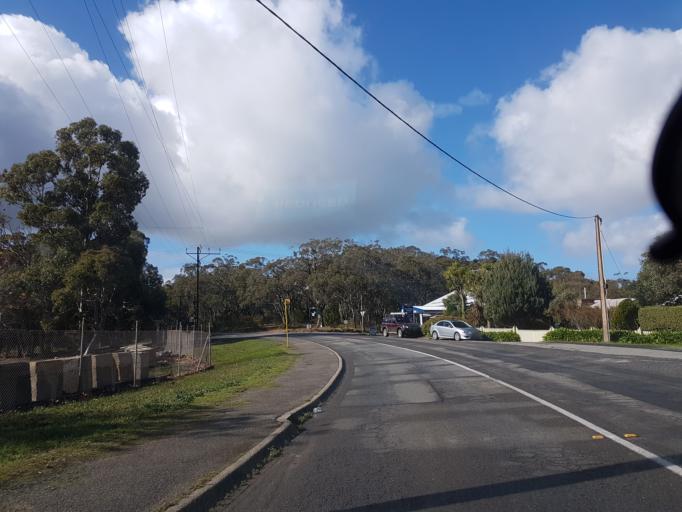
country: AU
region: South Australia
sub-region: Adelaide Hills
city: Heathfield
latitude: -35.0241
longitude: 138.7148
